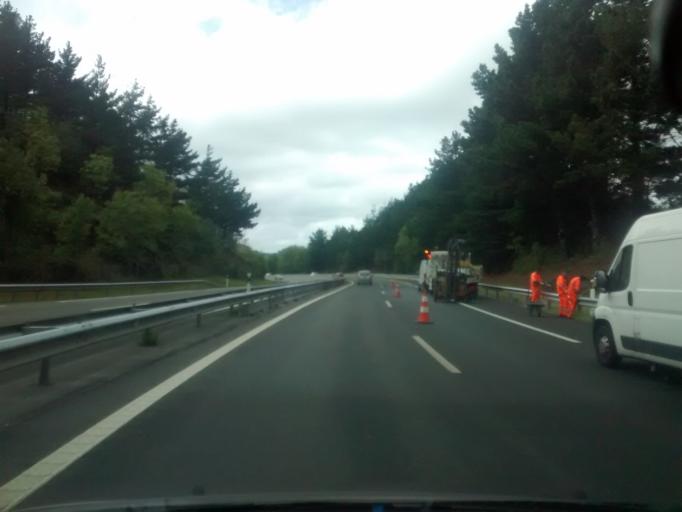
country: ES
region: Basque Country
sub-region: Provincia de Guipuzcoa
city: Deba
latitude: 43.2856
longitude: -2.3509
